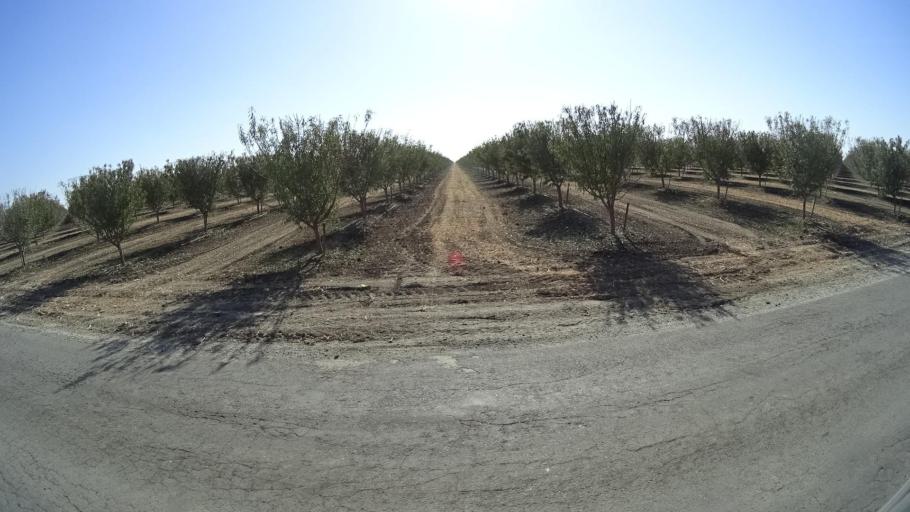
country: US
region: California
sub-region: Kern County
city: McFarland
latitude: 35.7034
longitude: -119.1984
